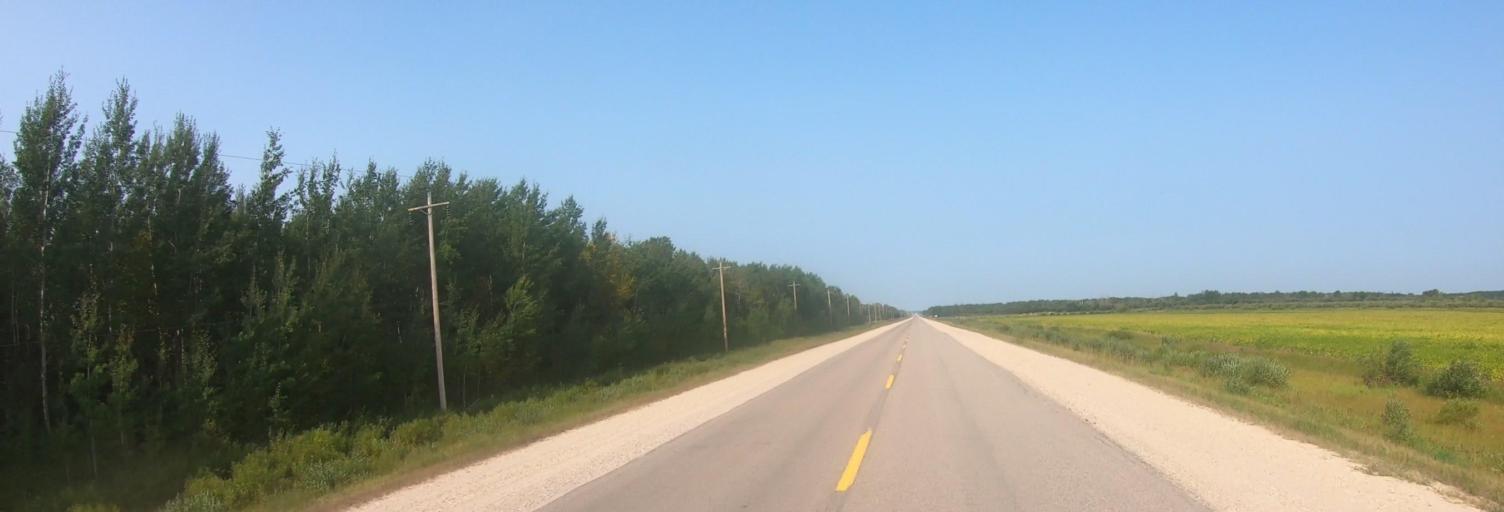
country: US
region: Minnesota
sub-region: Roseau County
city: Roseau
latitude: 49.0233
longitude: -95.6024
